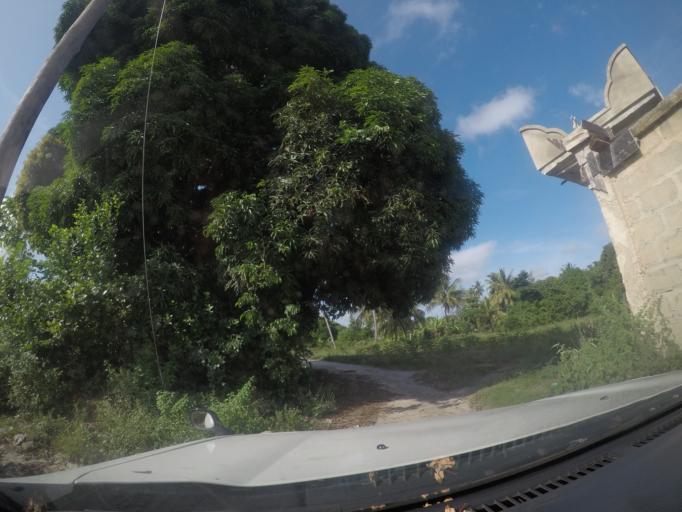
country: TZ
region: Pemba South
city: Chake Chake
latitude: -5.2490
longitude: 39.7835
